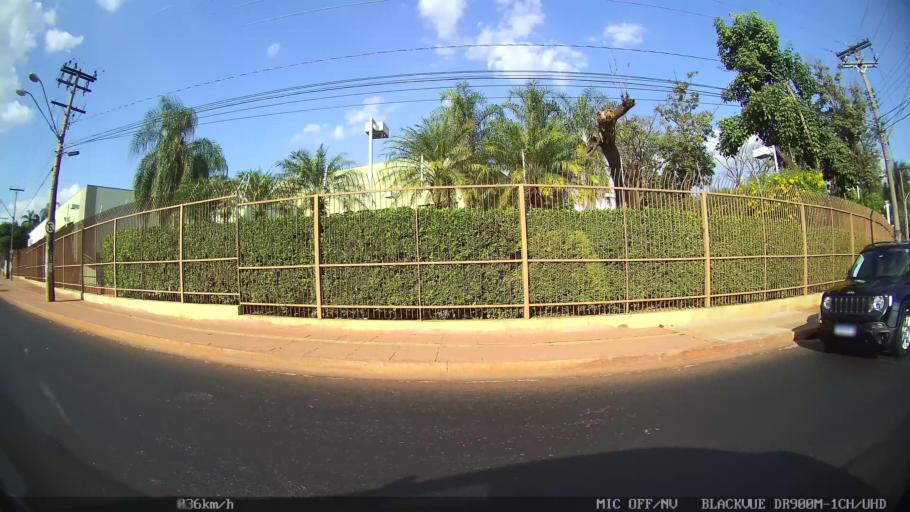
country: BR
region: Sao Paulo
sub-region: Ribeirao Preto
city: Ribeirao Preto
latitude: -21.1662
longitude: -47.8136
